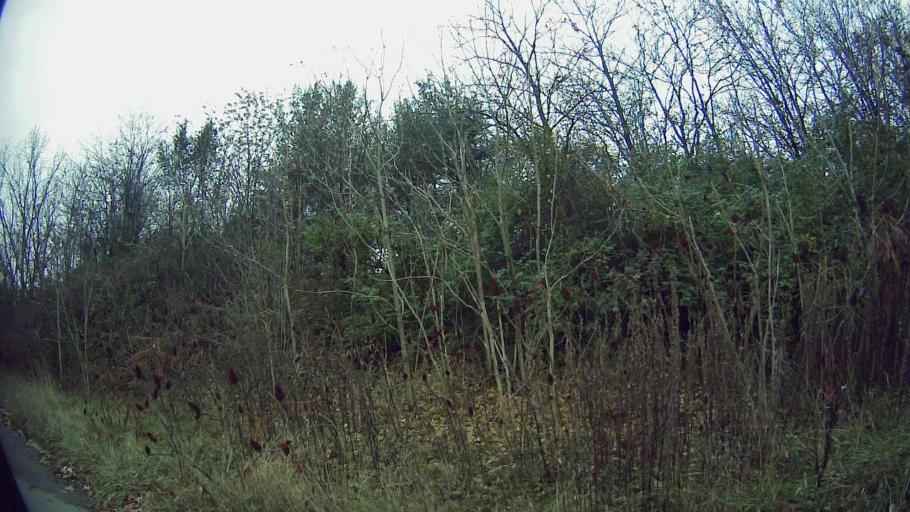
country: US
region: Michigan
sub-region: Wayne County
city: Dearborn
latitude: 42.3120
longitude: -83.2271
